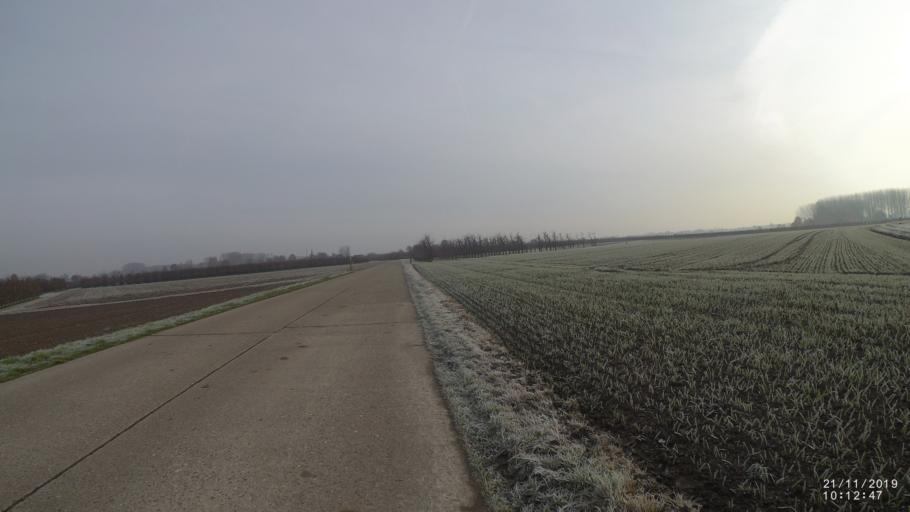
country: BE
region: Flanders
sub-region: Provincie Vlaams-Brabant
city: Zoutleeuw
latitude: 50.8190
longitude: 5.1179
